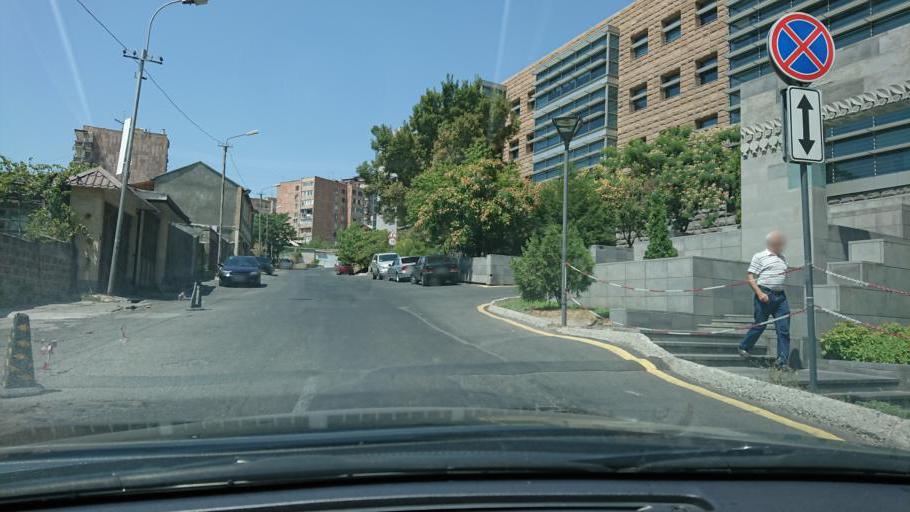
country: AM
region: Yerevan
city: Yerevan
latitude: 40.1932
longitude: 44.5039
